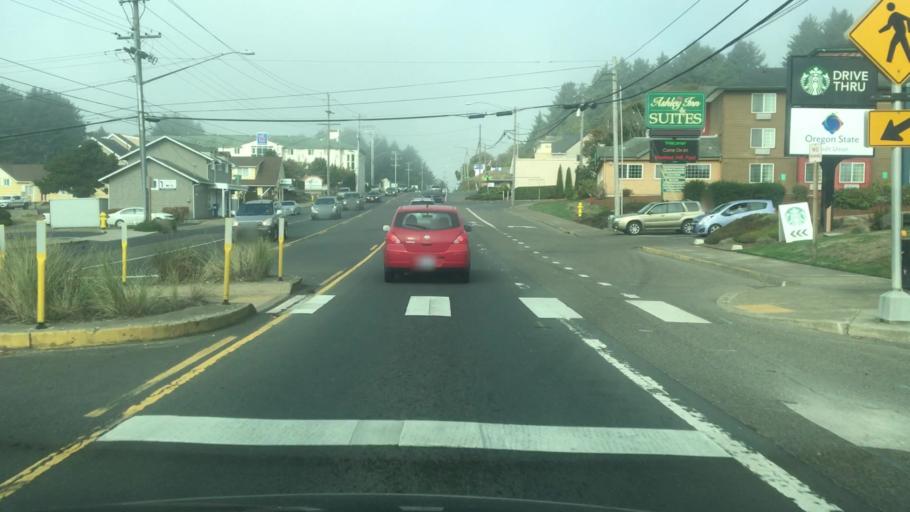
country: US
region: Oregon
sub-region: Lincoln County
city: Lincoln City
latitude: 44.9894
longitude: -124.0057
